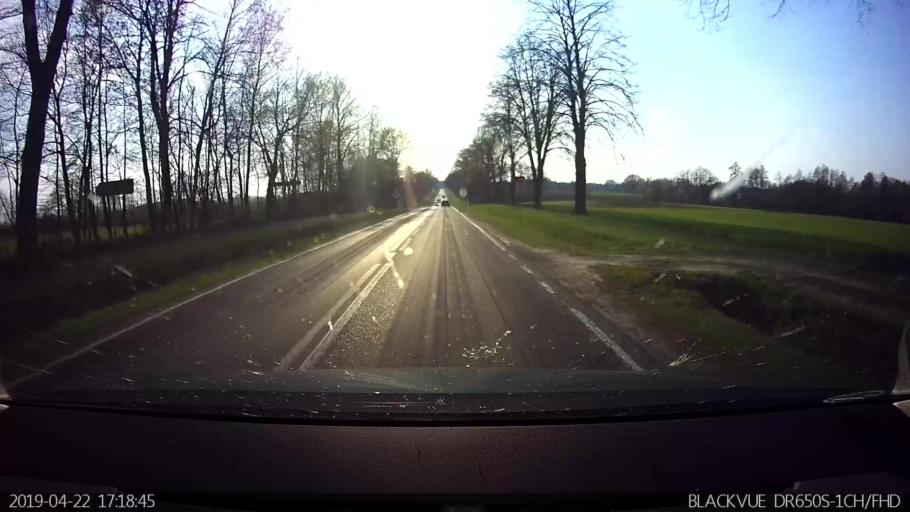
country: PL
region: Masovian Voivodeship
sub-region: Powiat sokolowski
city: Repki
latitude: 52.3849
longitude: 22.4078
